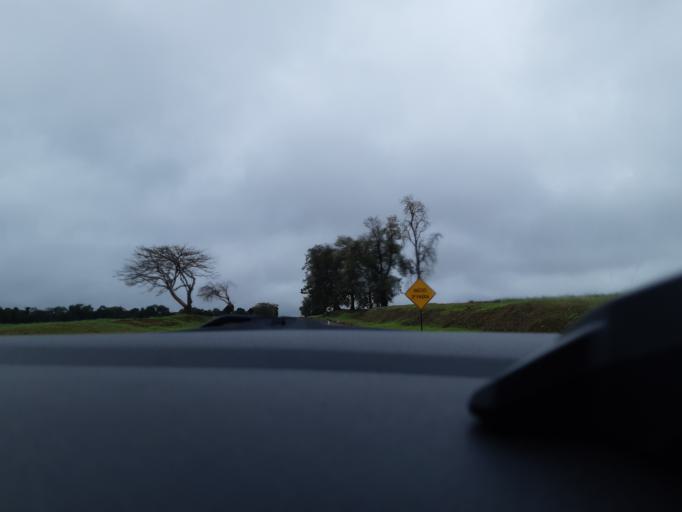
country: BR
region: Sao Paulo
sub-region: Ourinhos
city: Ourinhos
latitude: -23.0013
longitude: -49.9467
